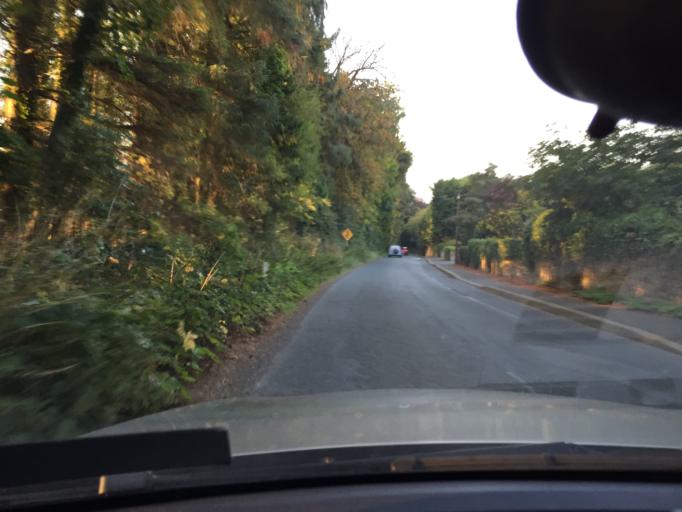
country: IE
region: Leinster
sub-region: Wicklow
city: Enniskerry
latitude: 53.1712
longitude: -6.1791
